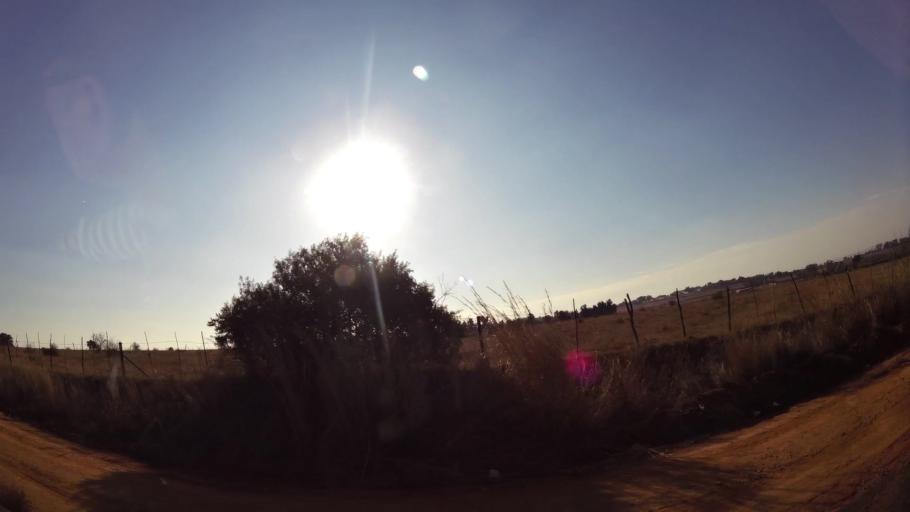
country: ZA
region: Gauteng
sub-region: West Rand District Municipality
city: Muldersdriseloop
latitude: -26.0101
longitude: 27.8942
